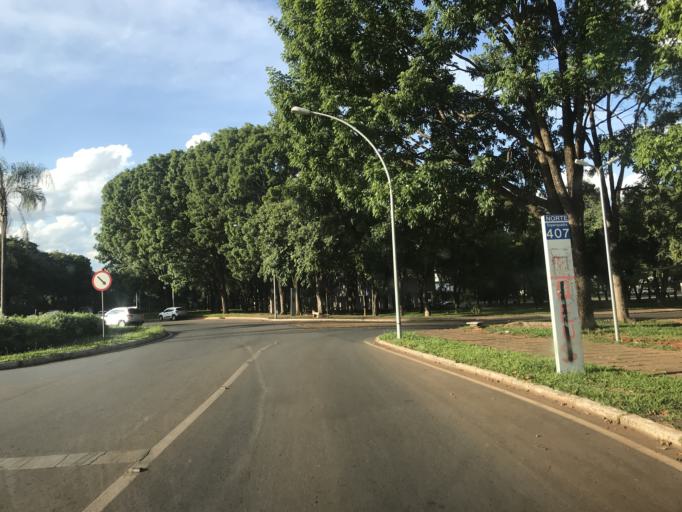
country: BR
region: Federal District
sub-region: Brasilia
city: Brasilia
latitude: -15.7636
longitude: -47.8798
